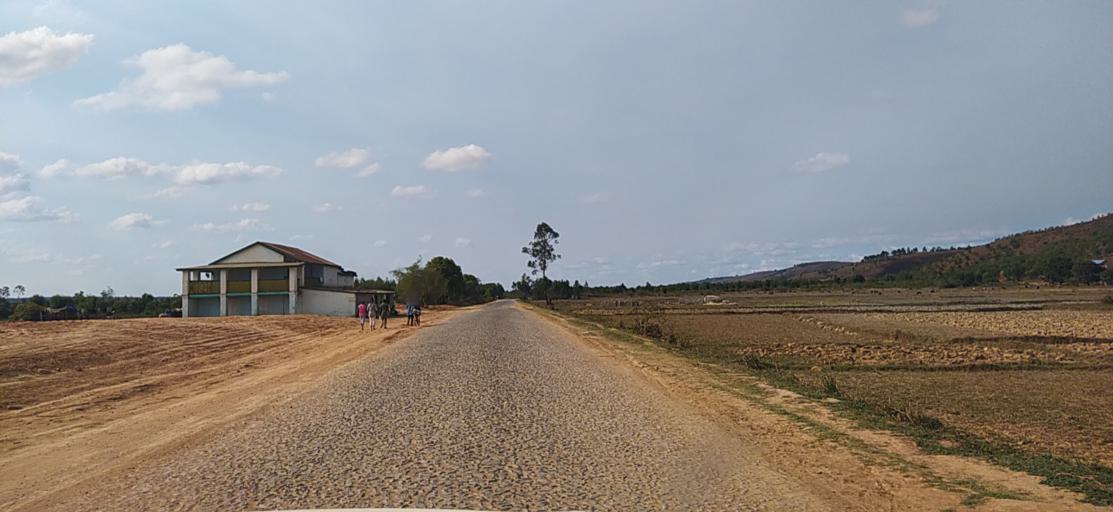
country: MG
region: Alaotra Mangoro
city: Moramanga
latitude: -18.6919
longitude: 48.2712
